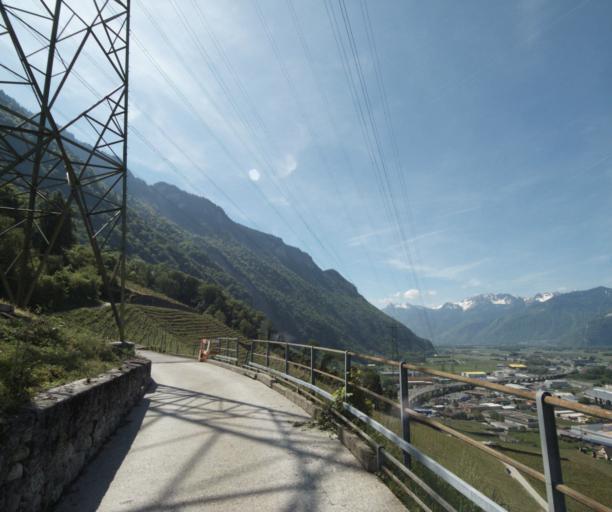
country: CH
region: Vaud
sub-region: Aigle District
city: Villeneuve
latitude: 46.3978
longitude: 6.9395
